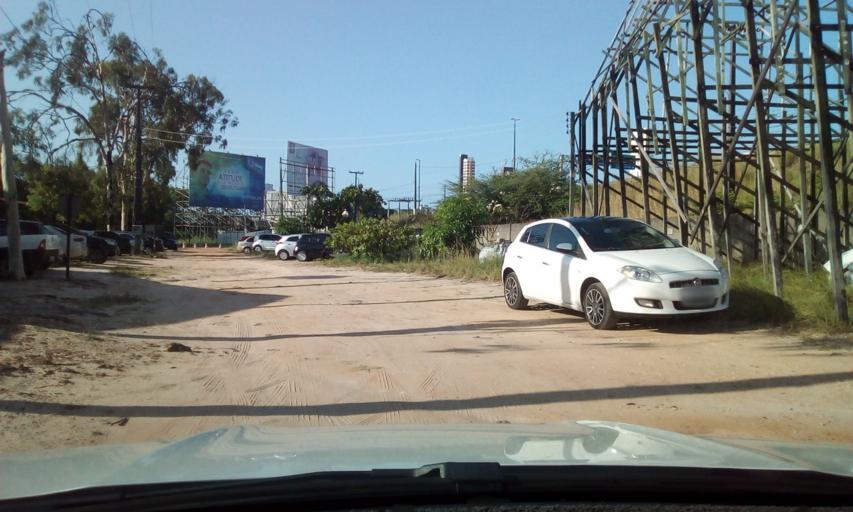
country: BR
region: Paraiba
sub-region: Joao Pessoa
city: Joao Pessoa
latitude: -7.1015
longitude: -34.8480
